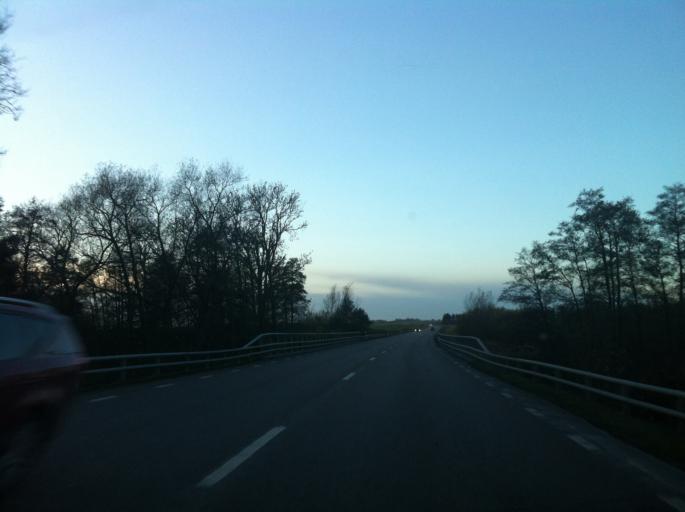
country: SE
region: Skane
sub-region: Eslovs Kommun
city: Eslov
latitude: 55.8655
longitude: 13.2403
